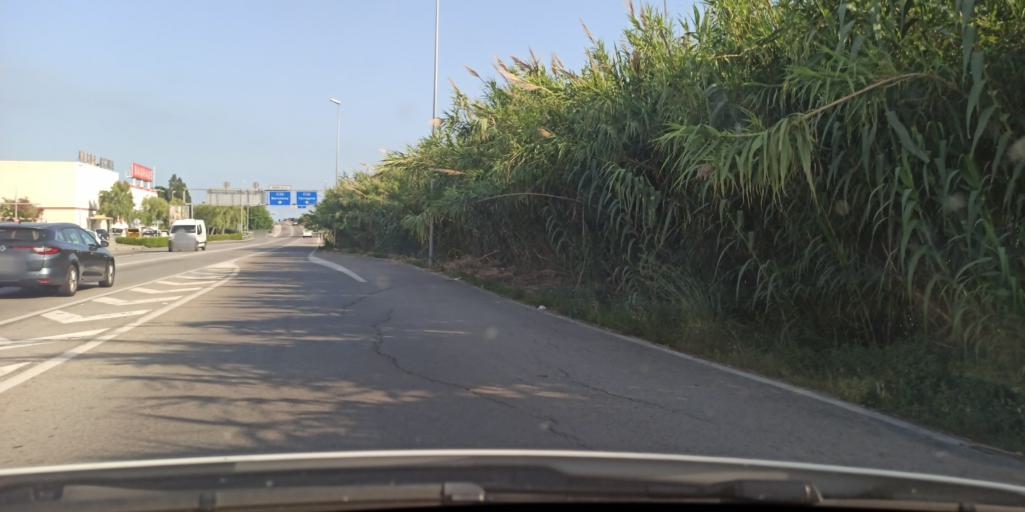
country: ES
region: Catalonia
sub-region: Provincia de Barcelona
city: Gava
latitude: 41.2955
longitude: 2.0064
